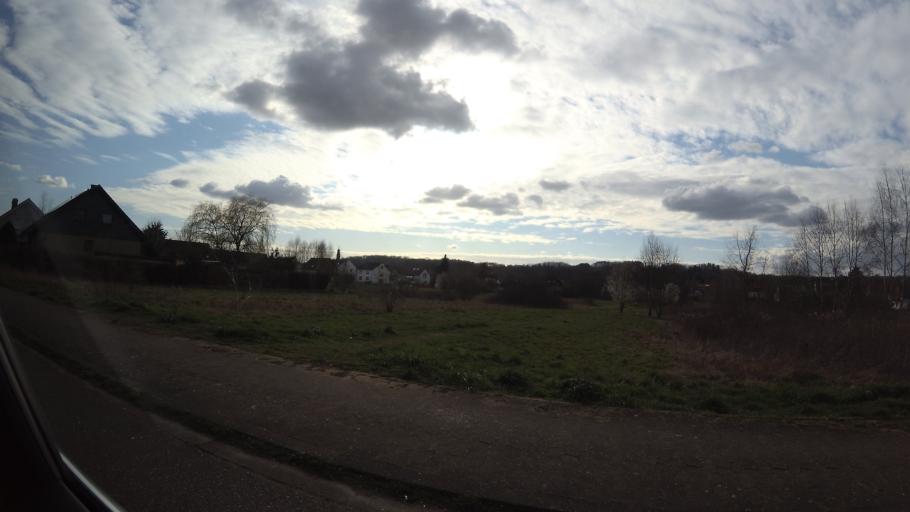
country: DE
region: Saarland
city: Blieskastel
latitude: 49.2298
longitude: 7.2709
